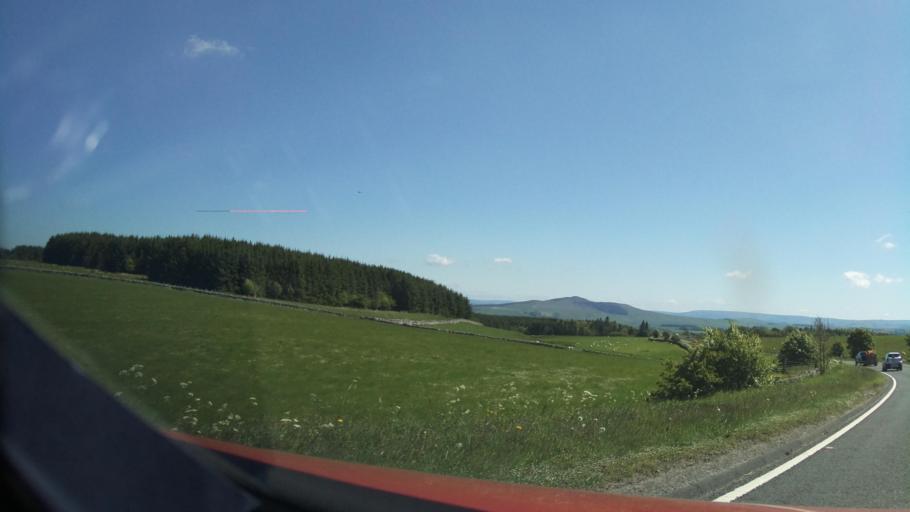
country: GB
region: Scotland
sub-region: The Scottish Borders
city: Hawick
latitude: 55.4631
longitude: -2.7866
